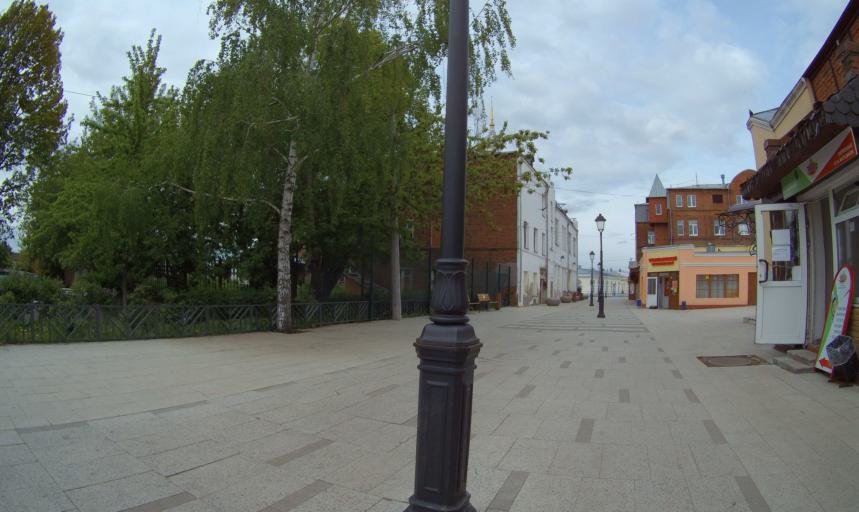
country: RU
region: Moskovskaya
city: Kolomna
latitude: 55.1006
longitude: 38.7541
